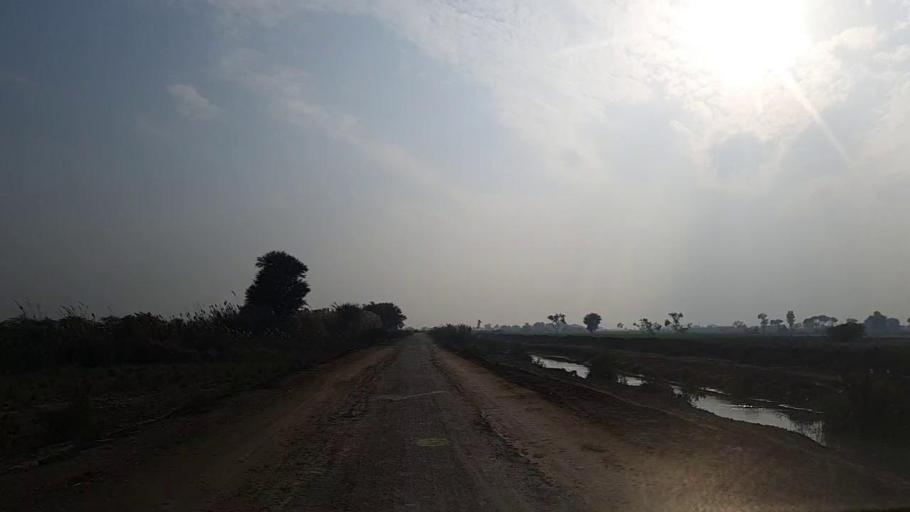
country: PK
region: Sindh
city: Jam Sahib
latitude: 26.3107
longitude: 68.5232
